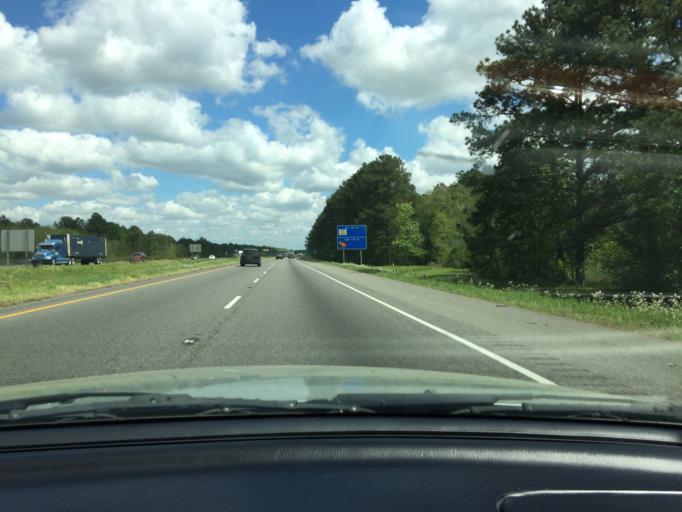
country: US
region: Louisiana
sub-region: Jefferson Davis Parish
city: Jennings
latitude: 30.2453
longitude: -92.6409
